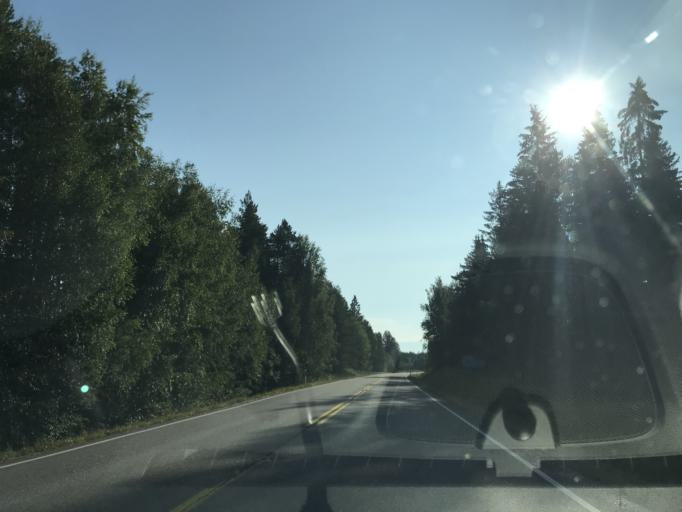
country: FI
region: Uusimaa
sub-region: Porvoo
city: Pukkila
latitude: 60.7689
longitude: 25.5159
